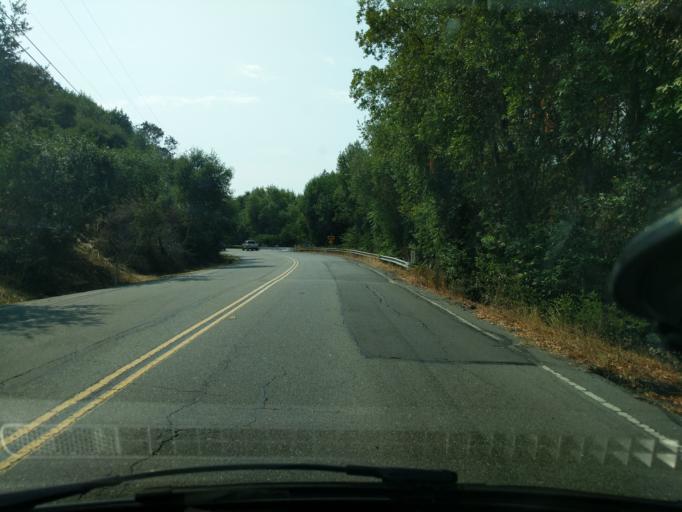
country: US
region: California
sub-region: Contra Costa County
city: San Ramon
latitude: 37.7670
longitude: -122.0127
